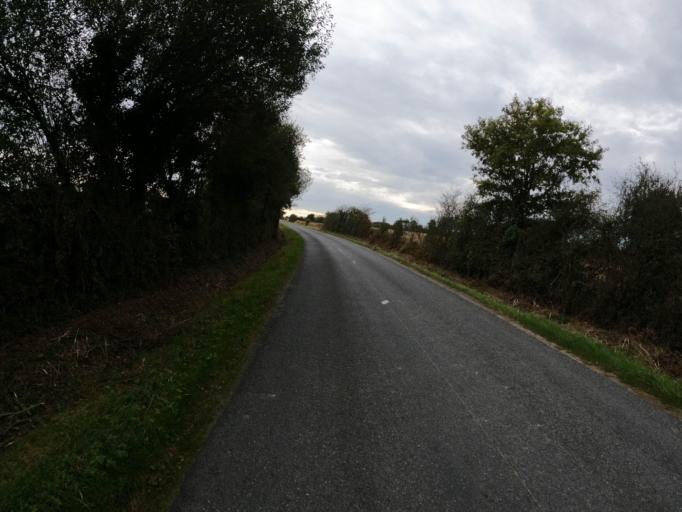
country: FR
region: Pays de la Loire
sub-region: Departement de Maine-et-Loire
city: Saint-Christophe-du-Bois
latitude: 47.0217
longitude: -0.9864
